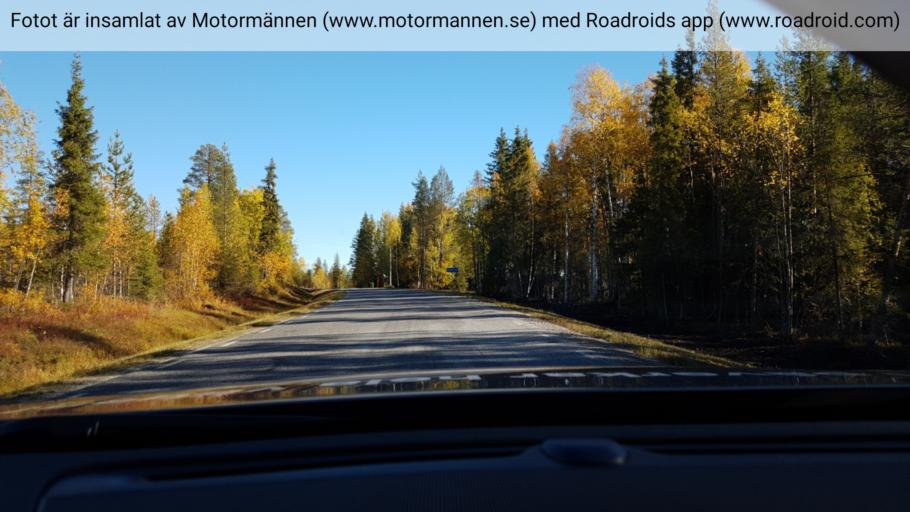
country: SE
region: Norrbotten
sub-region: Gallivare Kommun
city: Gaellivare
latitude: 66.4449
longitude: 20.7937
